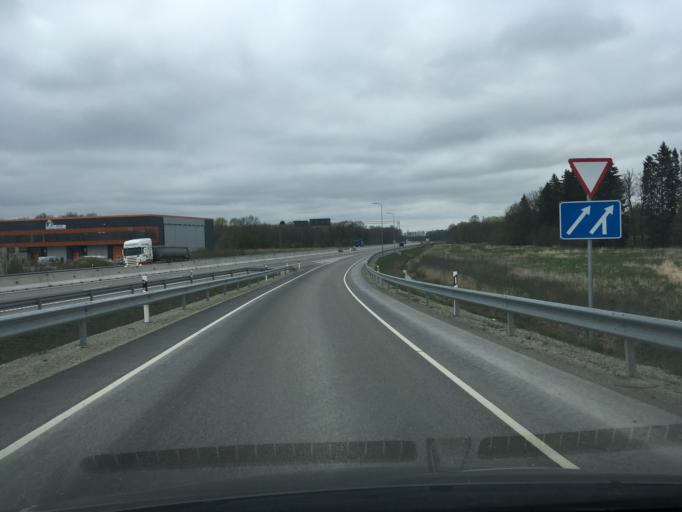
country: EE
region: Harju
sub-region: Rae vald
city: Jueri
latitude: 59.3730
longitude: 24.9111
